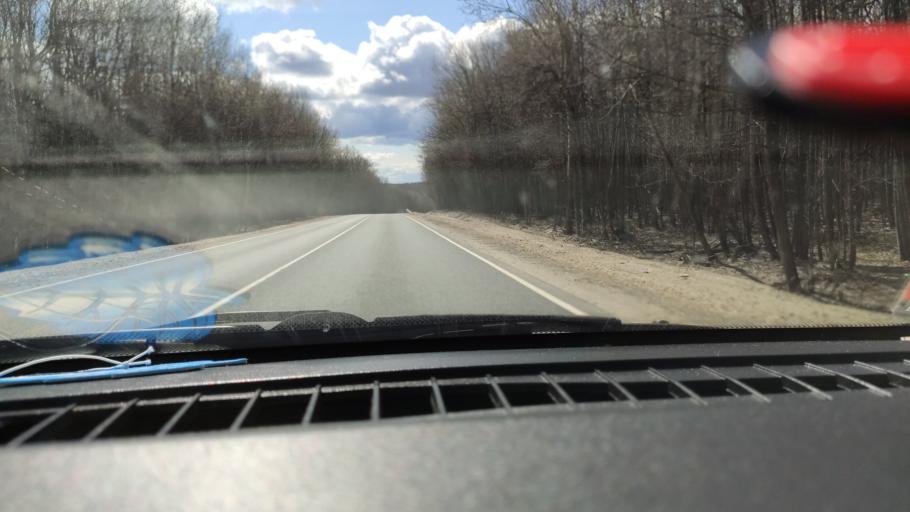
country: RU
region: Saratov
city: Khvalynsk
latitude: 52.4598
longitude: 48.0169
